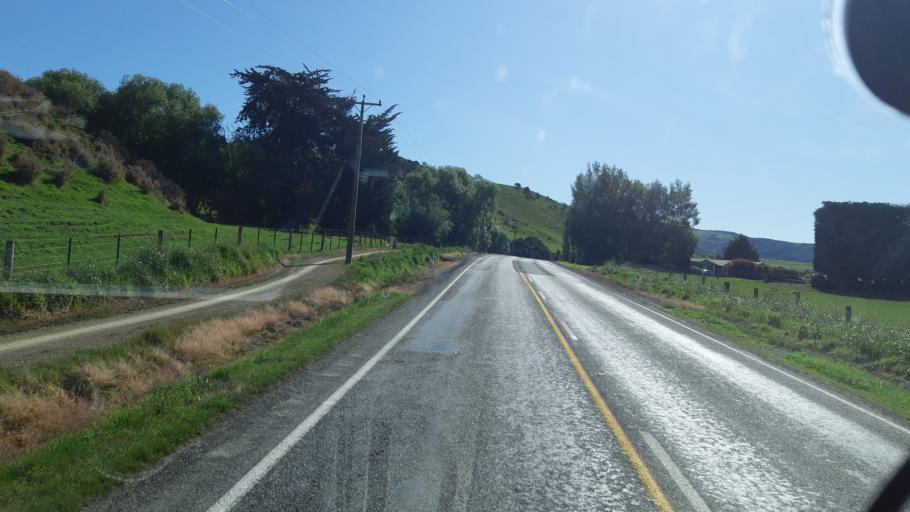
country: NZ
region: Otago
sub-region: Clutha District
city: Balclutha
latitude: -45.8283
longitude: 169.5472
